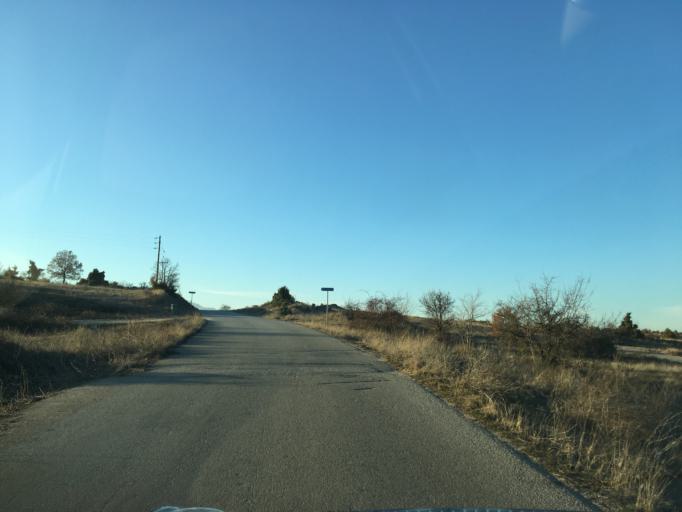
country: GR
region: West Macedonia
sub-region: Nomos Kozanis
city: Kozani
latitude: 40.2681
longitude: 21.7433
